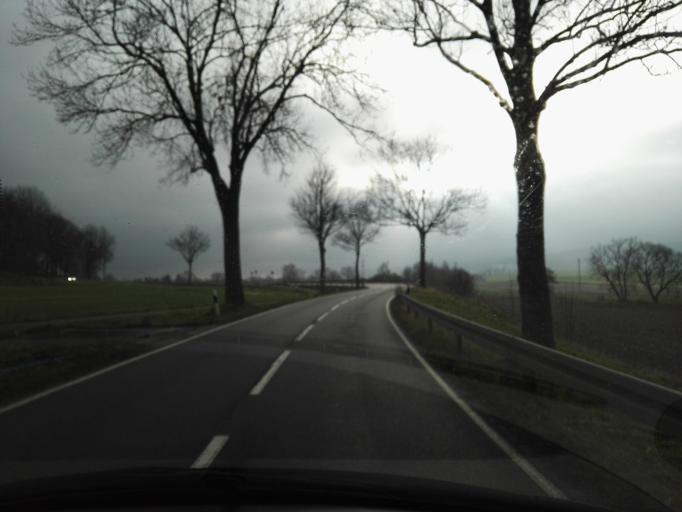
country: DE
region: Lower Saxony
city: Eberholzen
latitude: 52.0741
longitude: 9.8693
